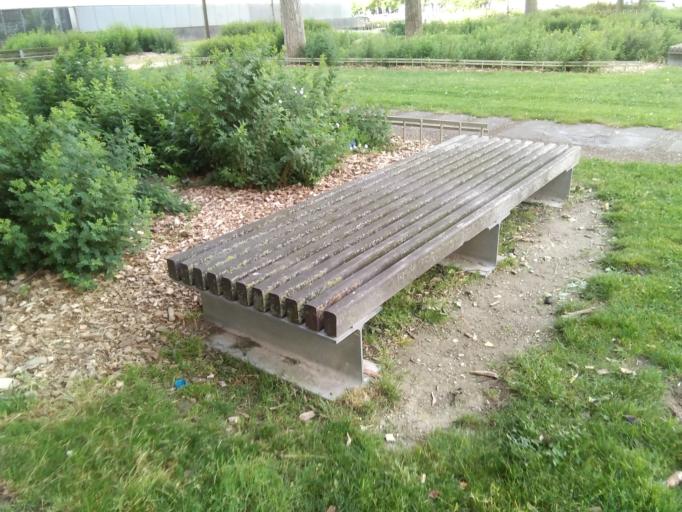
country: FR
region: Picardie
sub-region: Departement de la Somme
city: Amiens
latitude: 49.9122
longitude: 2.3070
